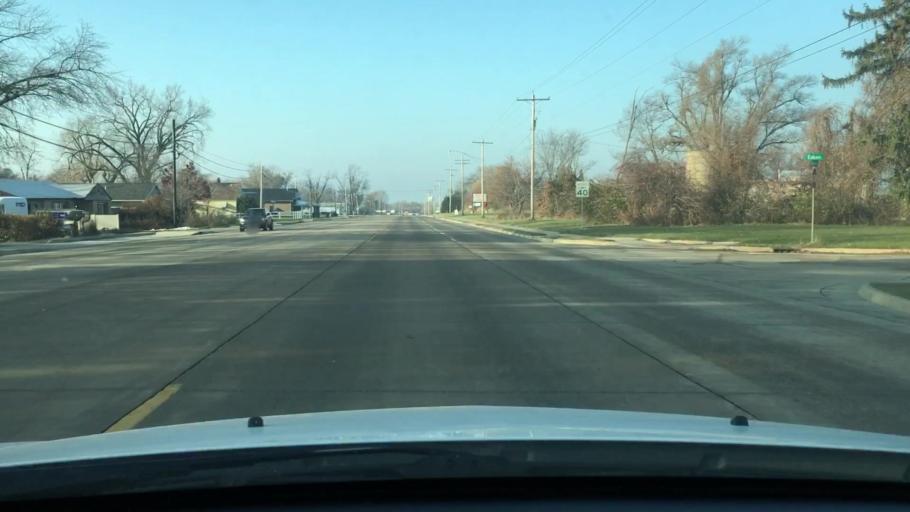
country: US
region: Illinois
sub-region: Tazewell County
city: Washington
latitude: 40.6983
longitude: -89.4663
